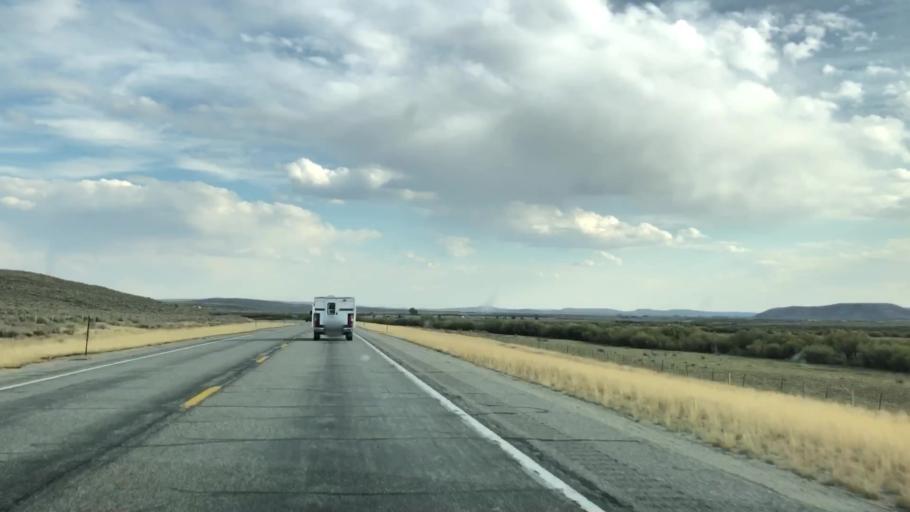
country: US
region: Wyoming
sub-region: Sublette County
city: Pinedale
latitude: 43.0248
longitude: -110.1241
